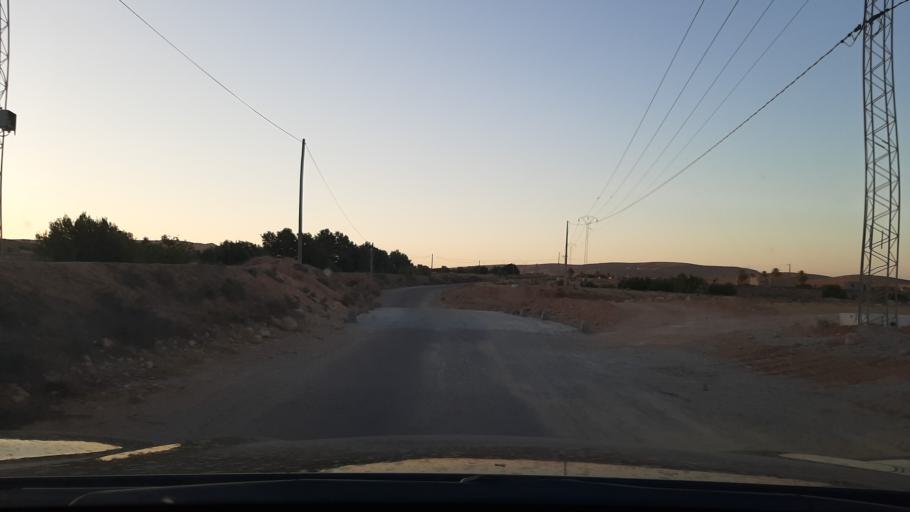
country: TN
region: Qabis
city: Matmata
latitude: 33.5537
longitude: 10.1862
